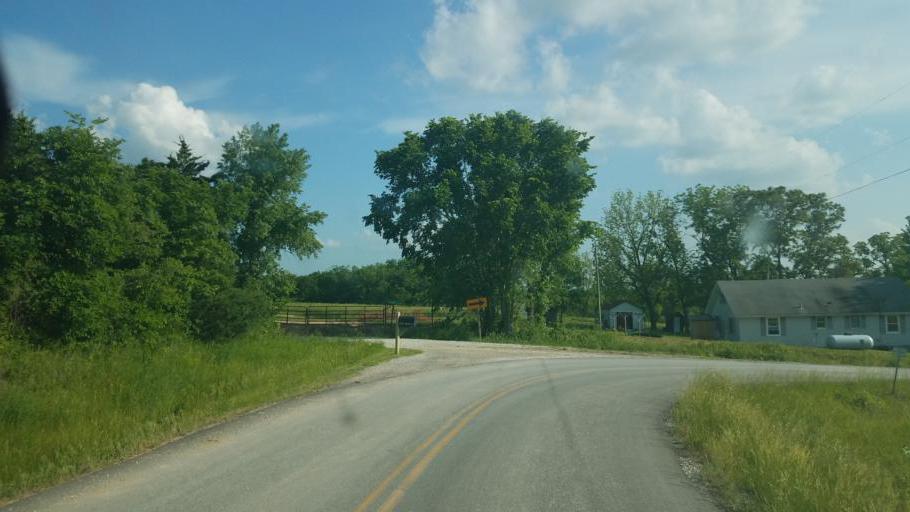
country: US
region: Missouri
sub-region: Moniteau County
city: California
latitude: 38.7603
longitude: -92.6053
